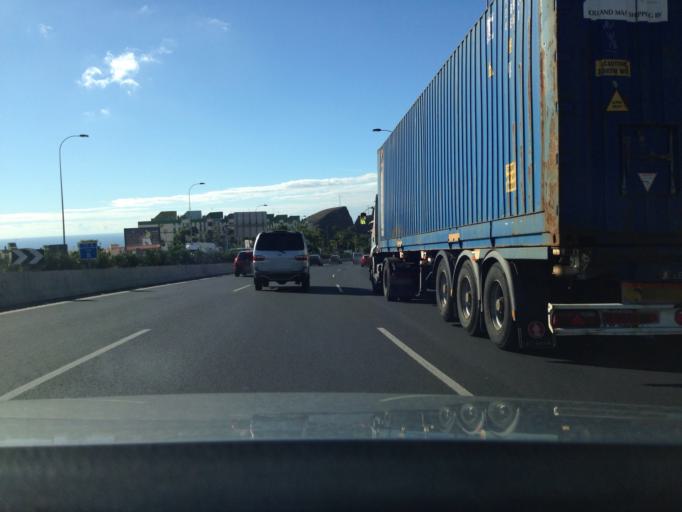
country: ES
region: Canary Islands
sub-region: Provincia de Santa Cruz de Tenerife
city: Santa Cruz de Tenerife
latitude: 28.4532
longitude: -16.2911
